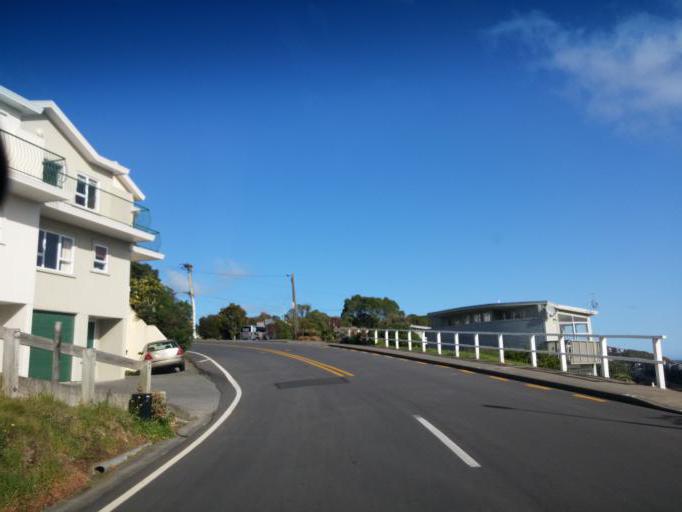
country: NZ
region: Wellington
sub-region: Wellington City
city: Wellington
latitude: -41.3212
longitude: 174.8241
